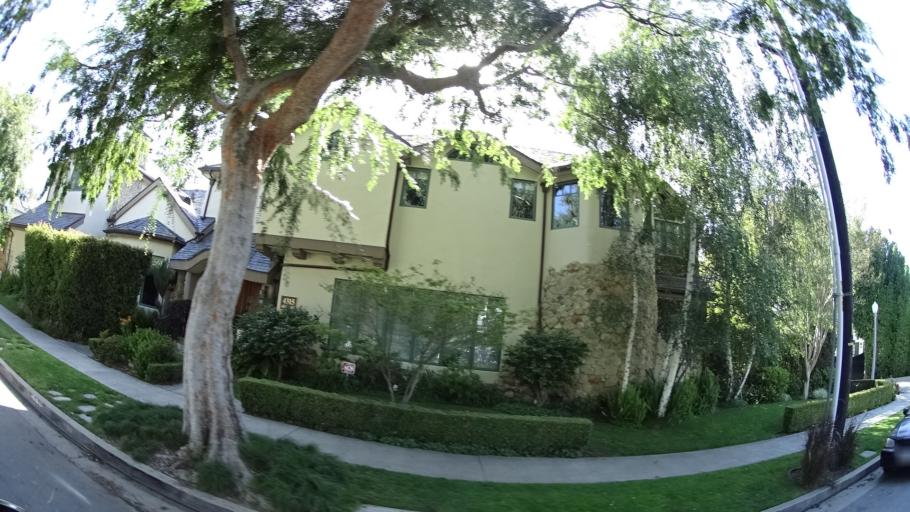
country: US
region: California
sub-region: Los Angeles County
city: Universal City
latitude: 34.1483
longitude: -118.3549
